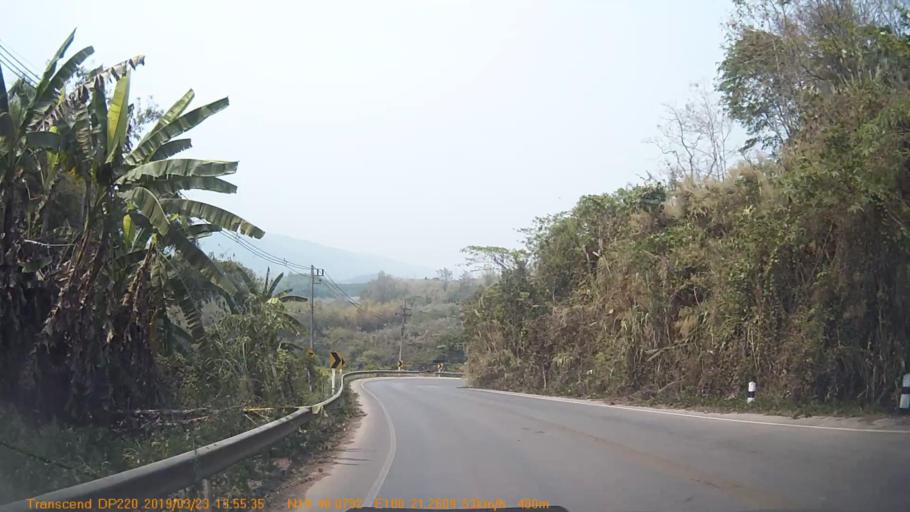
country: TH
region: Chiang Rai
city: Khun Tan
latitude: 19.8017
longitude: 100.3545
